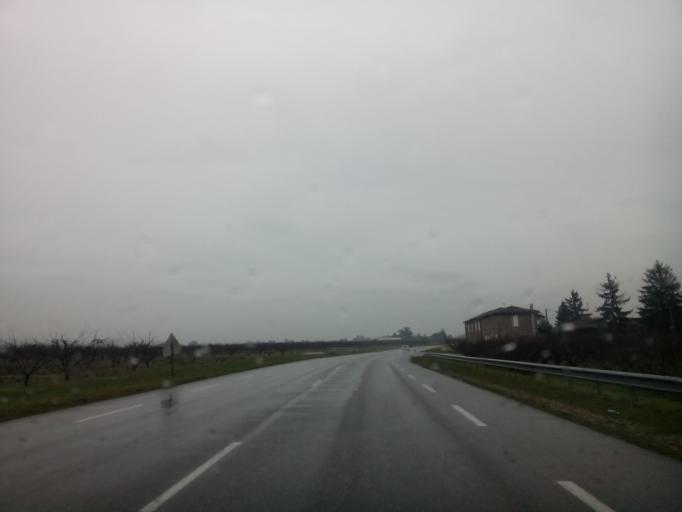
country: FR
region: Rhone-Alpes
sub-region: Departement de la Drome
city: Clerieux
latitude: 45.0542
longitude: 4.9717
